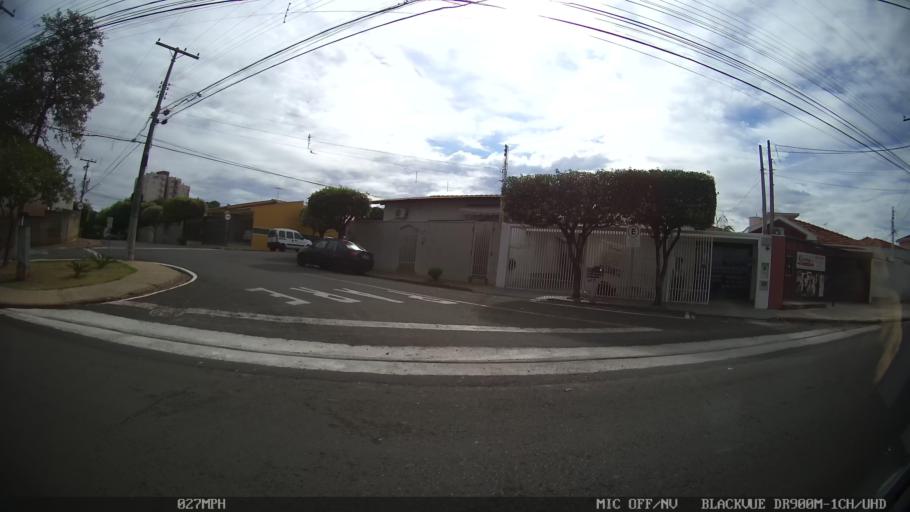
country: BR
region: Sao Paulo
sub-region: Sao Jose Do Rio Preto
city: Sao Jose do Rio Preto
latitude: -20.8165
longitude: -49.3624
